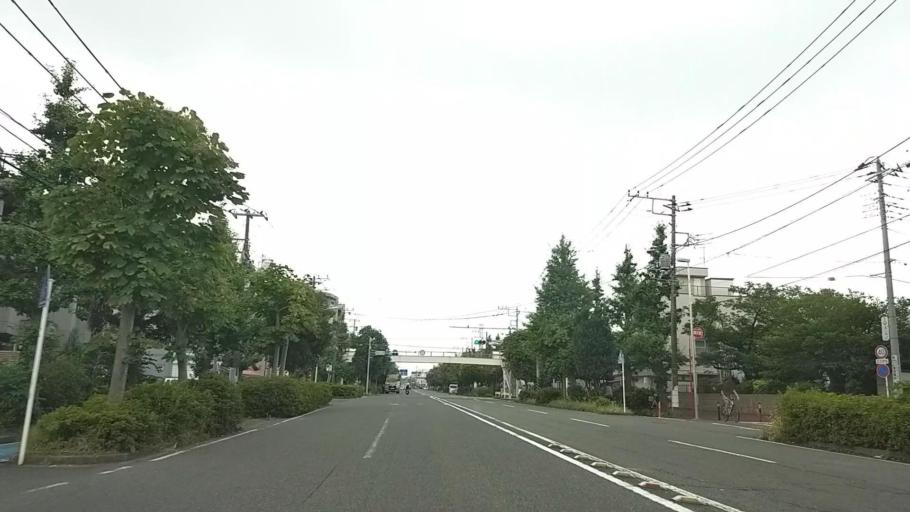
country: JP
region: Kanagawa
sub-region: Kawasaki-shi
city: Kawasaki
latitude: 35.5188
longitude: 139.7102
